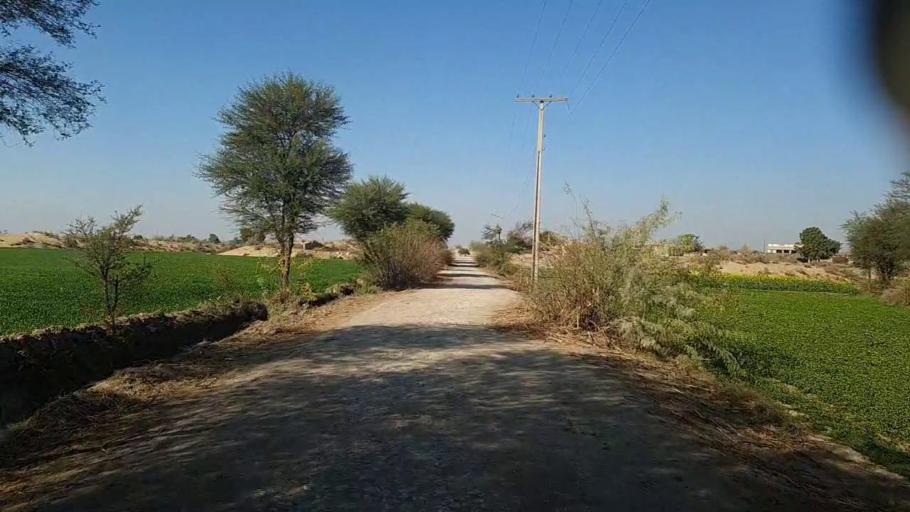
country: PK
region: Sindh
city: Khairpur
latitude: 27.9202
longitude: 69.7509
